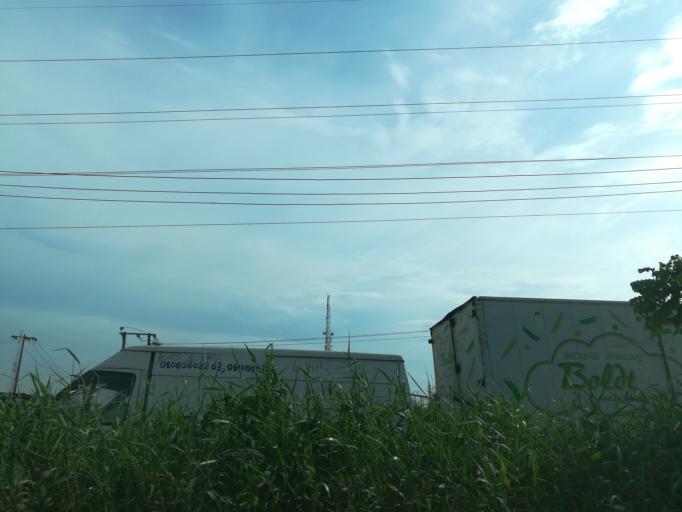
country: NG
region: Lagos
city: Ojota
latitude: 6.6105
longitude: 3.4206
